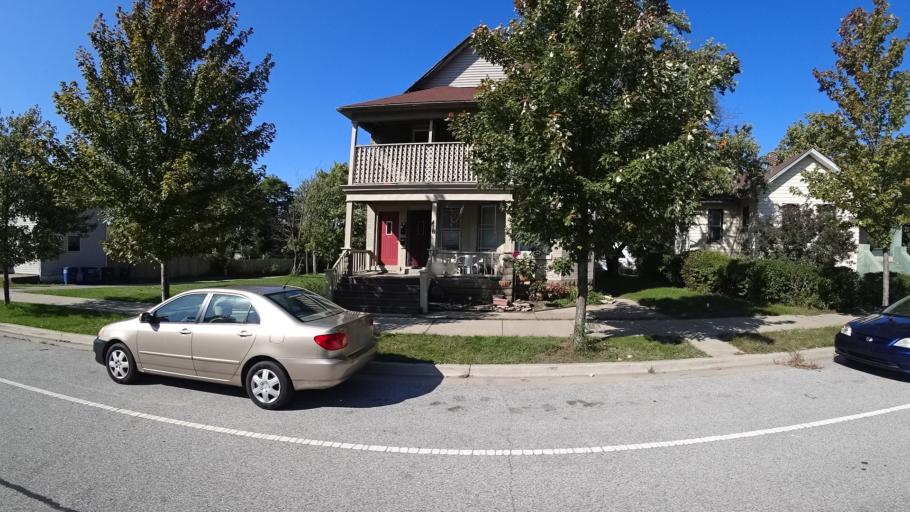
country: US
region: Indiana
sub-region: LaPorte County
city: Michigan City
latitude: 41.7143
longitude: -86.8946
